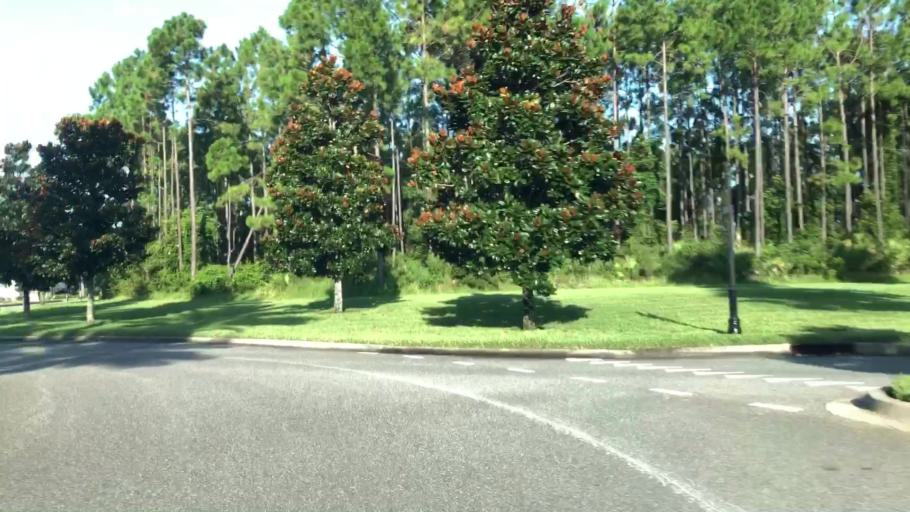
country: US
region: Florida
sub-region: Saint Johns County
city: Palm Valley
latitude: 30.1116
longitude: -81.4214
